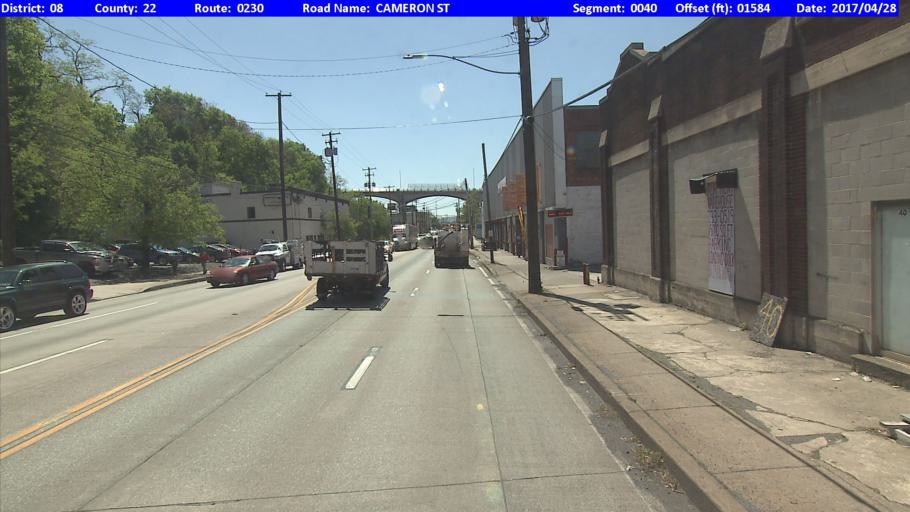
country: US
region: Pennsylvania
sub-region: Dauphin County
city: Harrisburg
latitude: 40.2638
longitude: -76.8743
